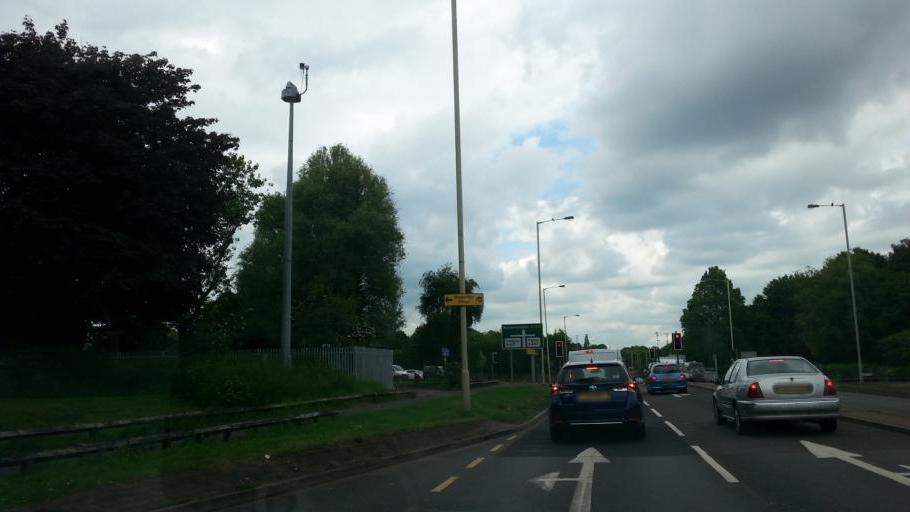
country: GB
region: England
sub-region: Sandwell
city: Tipton
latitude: 52.5308
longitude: -2.0860
